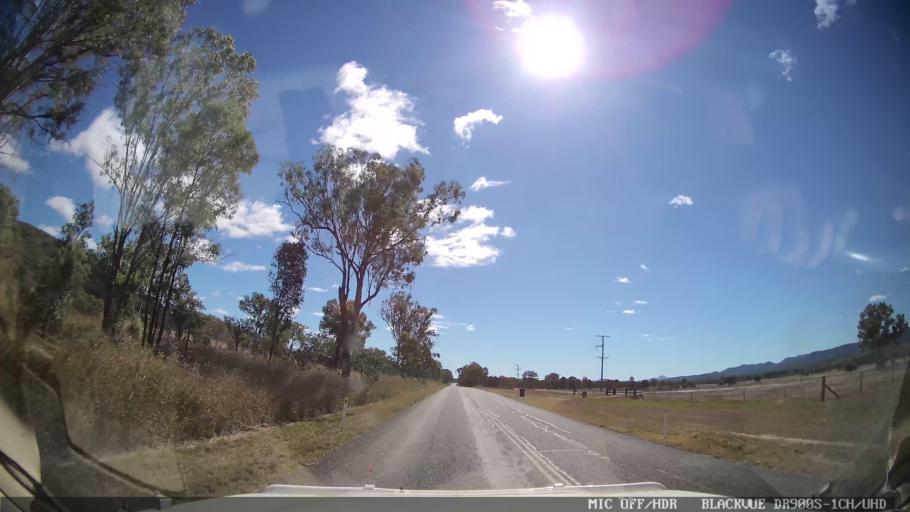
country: AU
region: Queensland
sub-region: Gladstone
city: Toolooa
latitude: -24.4506
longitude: 151.3452
